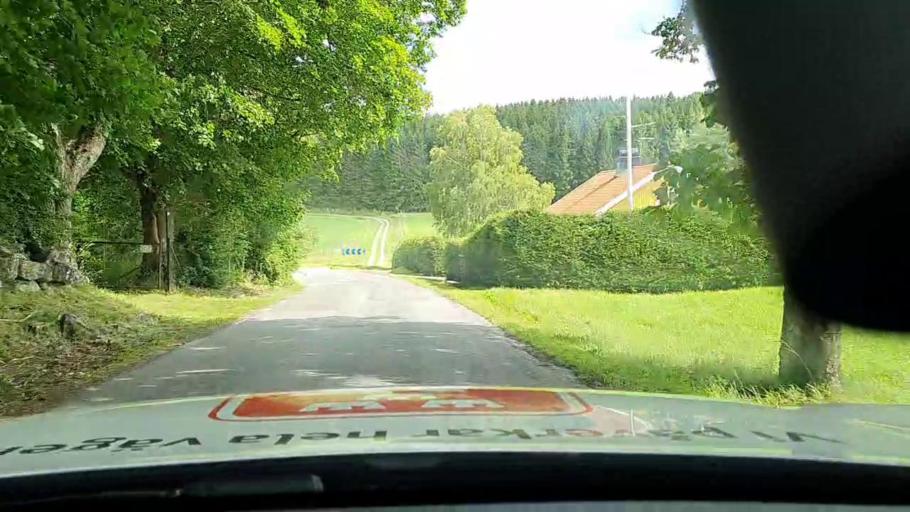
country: SE
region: Vaestra Goetaland
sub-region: Karlsborgs Kommun
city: Molltorp
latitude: 58.6030
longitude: 14.3109
